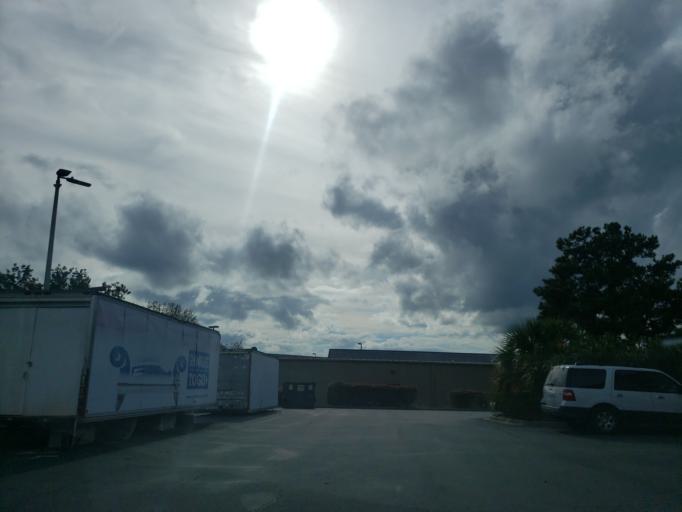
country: US
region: Georgia
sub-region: Chatham County
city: Georgetown
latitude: 32.0021
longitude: -81.2828
